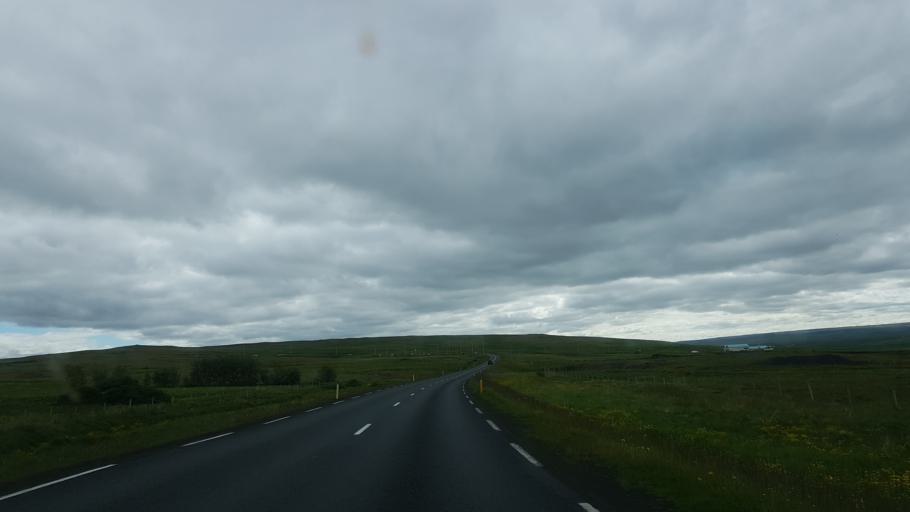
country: IS
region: Northwest
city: Saudarkrokur
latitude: 65.3589
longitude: -20.8898
